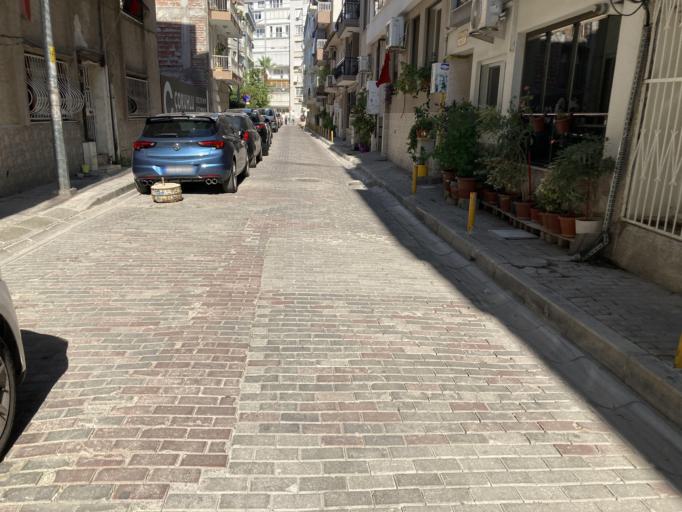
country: TR
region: Izmir
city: Karsiyaka
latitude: 38.4570
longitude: 27.1230
